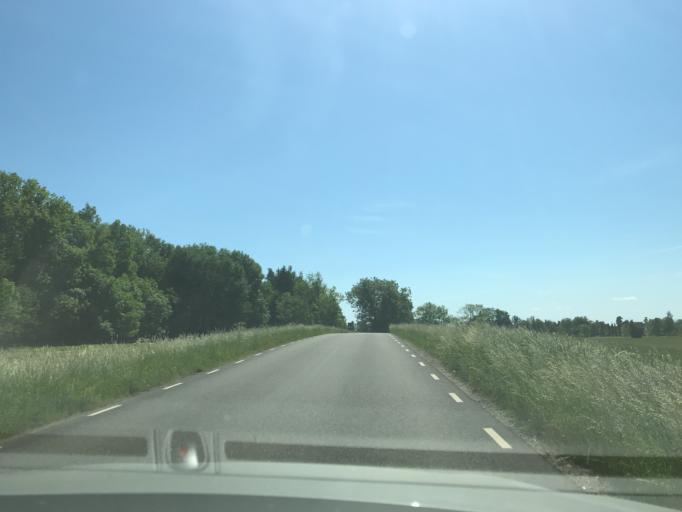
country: SE
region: Vaestra Goetaland
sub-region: Gotene Kommun
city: Kallby
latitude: 58.5400
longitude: 13.3254
